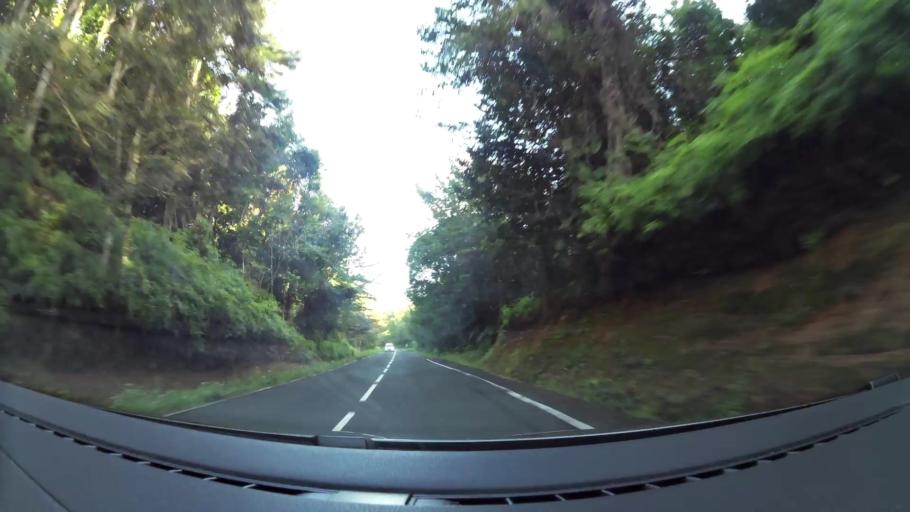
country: GP
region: Guadeloupe
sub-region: Guadeloupe
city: Bouillante
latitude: 16.1769
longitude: -61.7037
